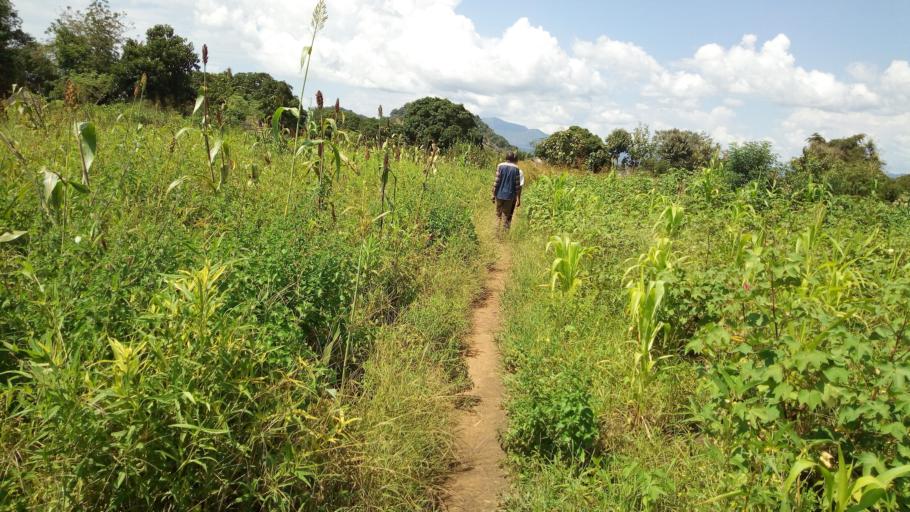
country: UG
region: Northern Region
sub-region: Adjumani District
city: Adjumani
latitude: 3.4607
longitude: 31.8984
